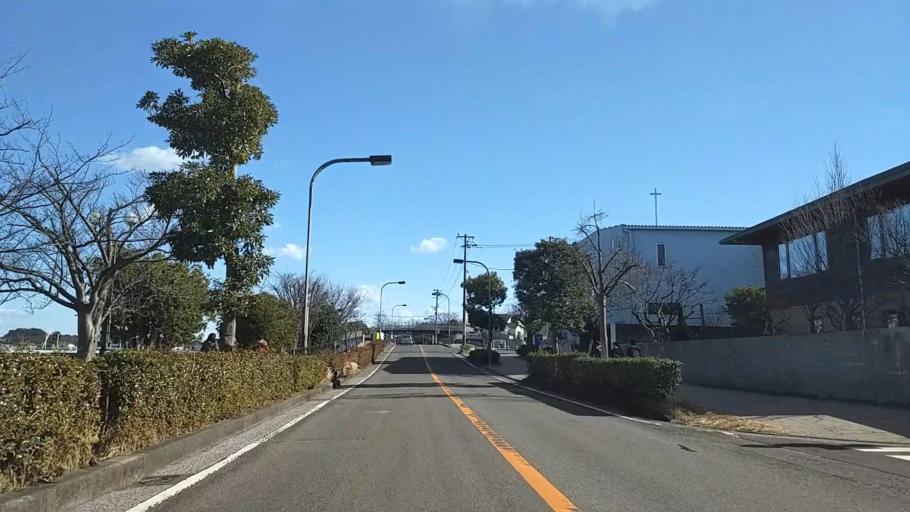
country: JP
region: Kanagawa
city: Yokosuka
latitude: 35.3268
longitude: 139.6281
